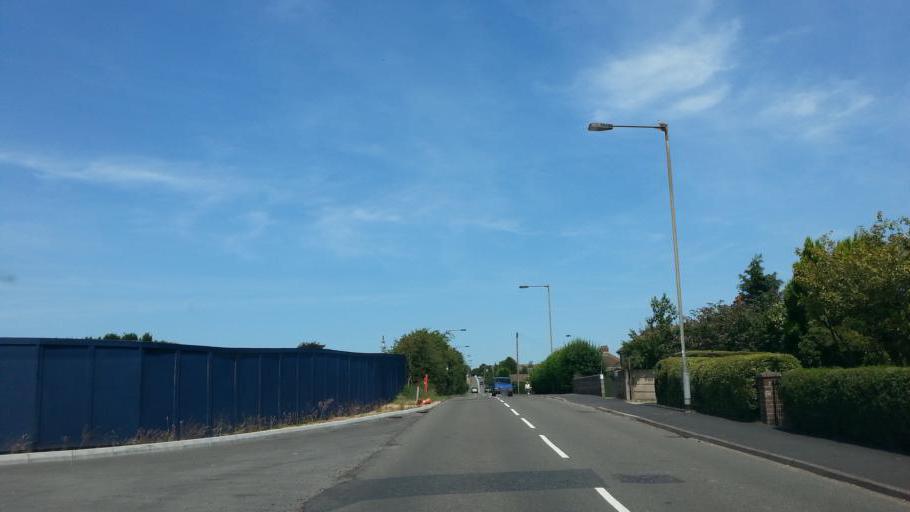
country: GB
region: England
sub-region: Staffordshire
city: Cannock
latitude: 52.7157
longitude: -2.0226
